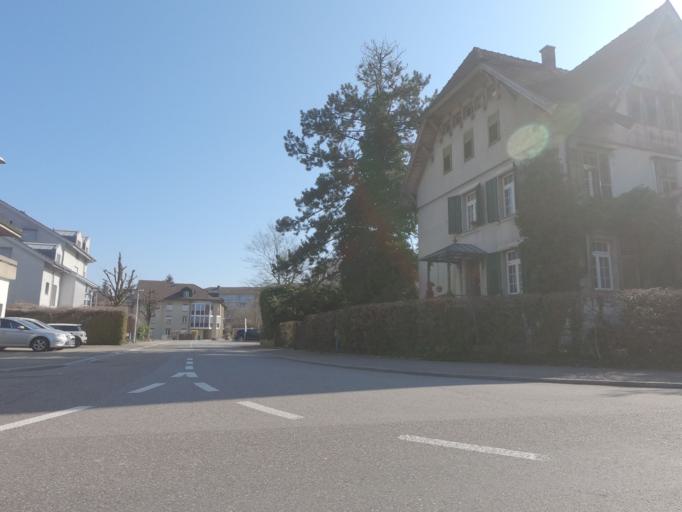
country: CH
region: Solothurn
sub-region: Bezirk Wasseramt
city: Zuchwil
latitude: 47.2042
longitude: 7.5570
